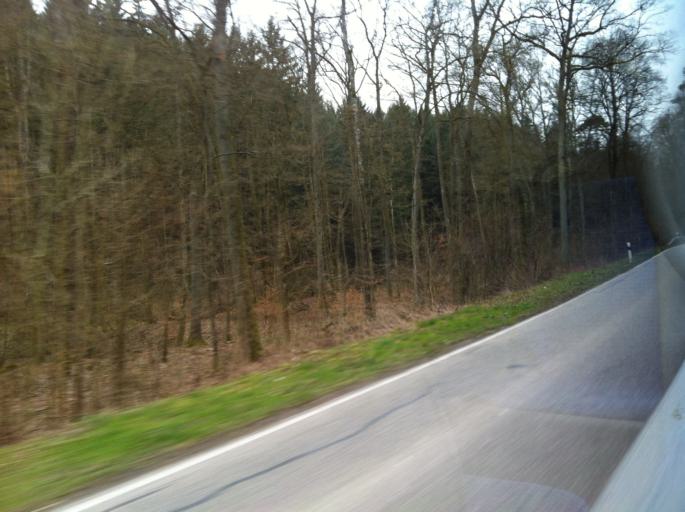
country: DE
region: Baden-Wuerttemberg
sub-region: Karlsruhe Region
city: Mosbach
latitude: 49.3786
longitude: 9.1550
